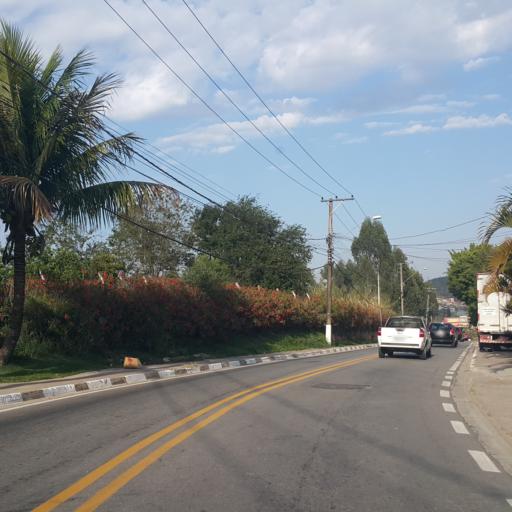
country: BR
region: Sao Paulo
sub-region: Louveira
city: Louveira
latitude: -23.0833
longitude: -46.9713
